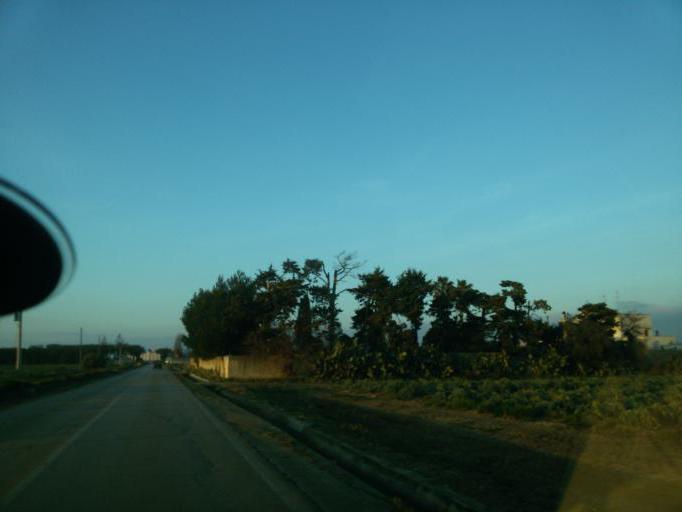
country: IT
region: Apulia
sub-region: Provincia di Brindisi
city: La Rosa
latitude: 40.6071
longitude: 17.9448
